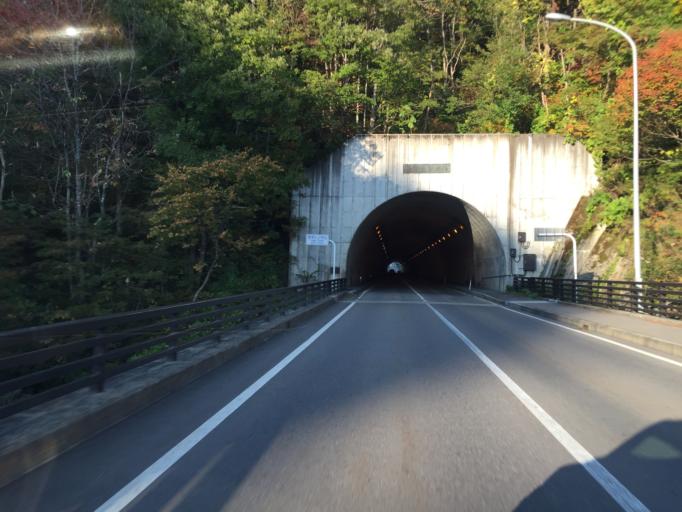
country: JP
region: Fukushima
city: Kitakata
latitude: 37.7510
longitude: 139.8969
